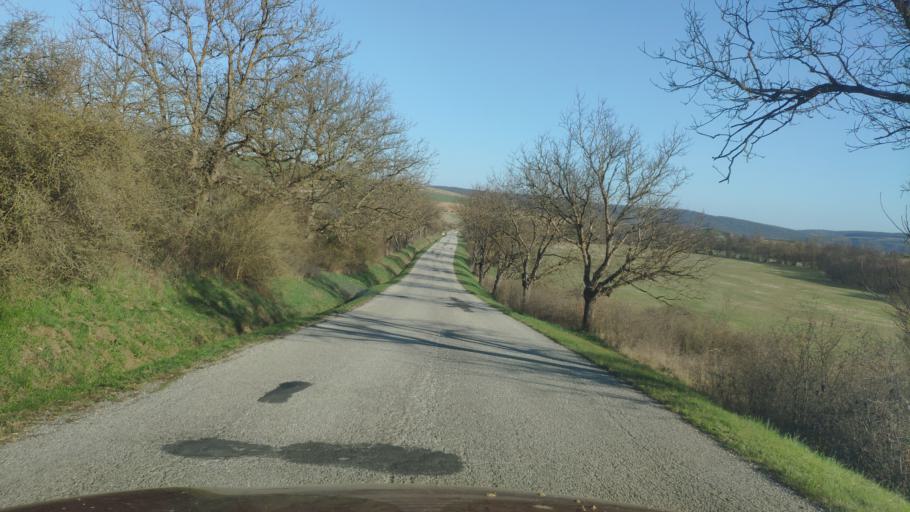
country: SK
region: Banskobystricky
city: Revuca
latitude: 48.4972
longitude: 20.2609
